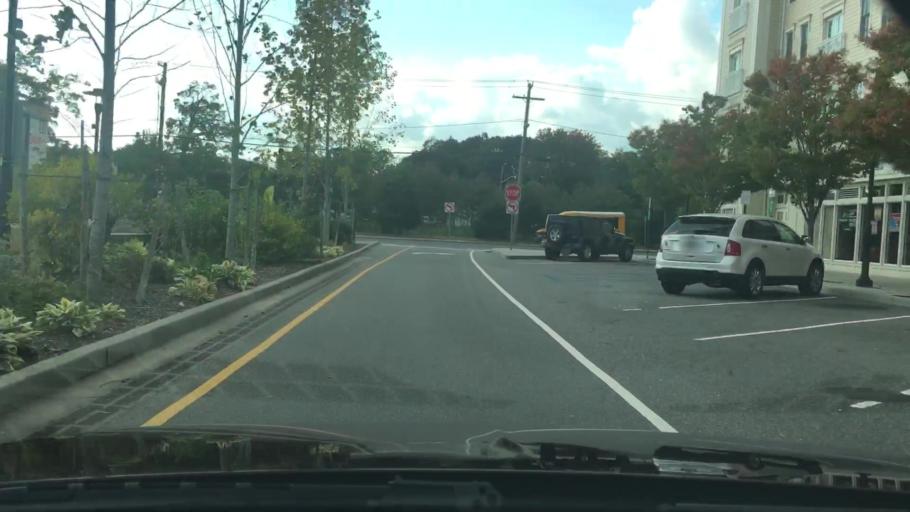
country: US
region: New York
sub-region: Suffolk County
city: Wyandanch
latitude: 40.7557
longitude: -73.3589
